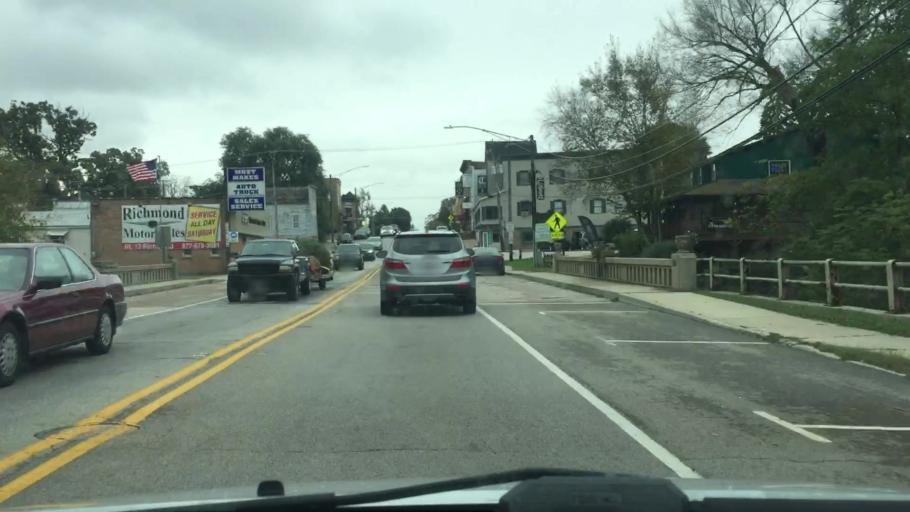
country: US
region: Illinois
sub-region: McHenry County
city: Richmond
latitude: 42.4775
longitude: -88.3061
